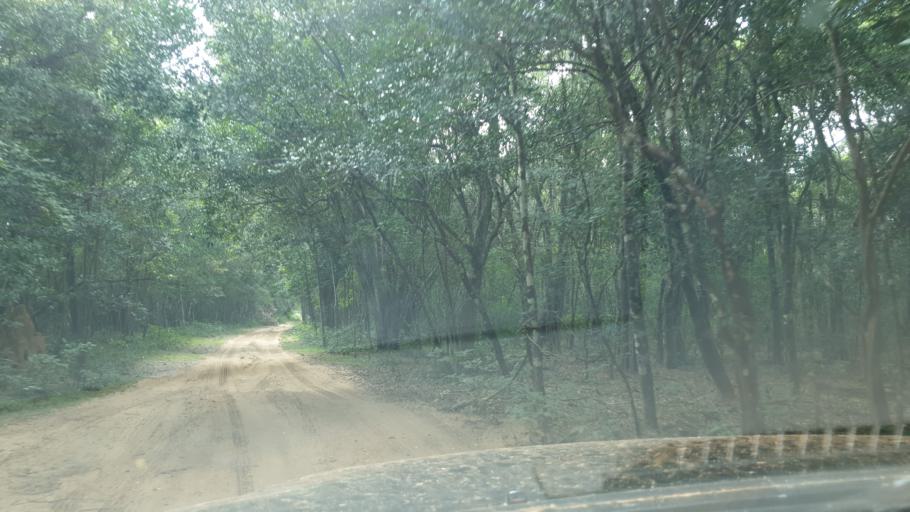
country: LK
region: North Central
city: Anuradhapura
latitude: 8.4194
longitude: 80.0105
